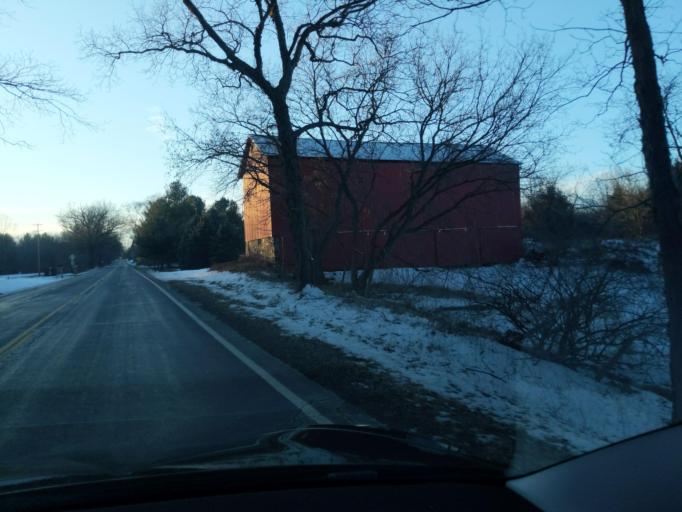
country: US
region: Michigan
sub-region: Ingham County
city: Stockbridge
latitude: 42.5342
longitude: -84.2842
